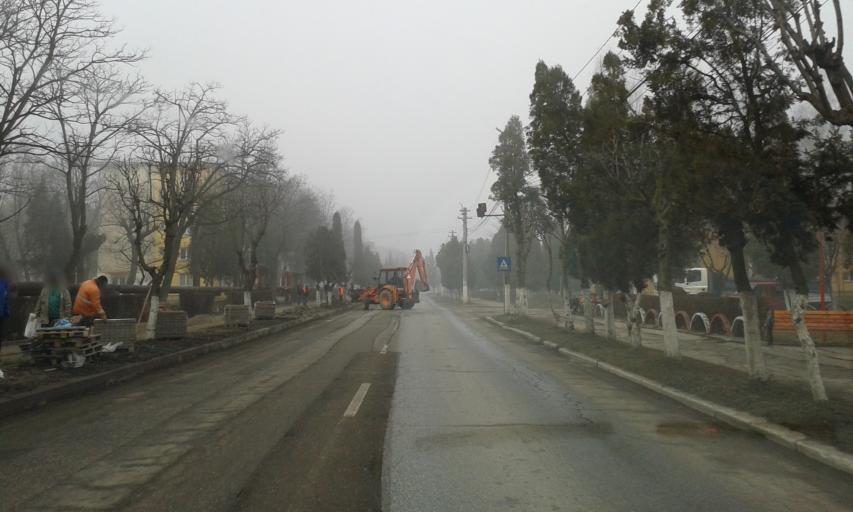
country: RO
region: Hunedoara
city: Vulcan
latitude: 45.3767
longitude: 23.2927
